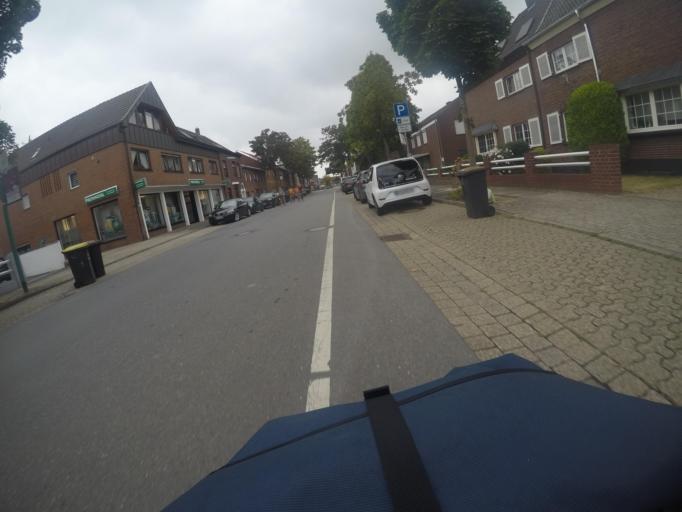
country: DE
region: North Rhine-Westphalia
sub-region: Regierungsbezirk Dusseldorf
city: Weeze
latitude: 51.6242
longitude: 6.2026
